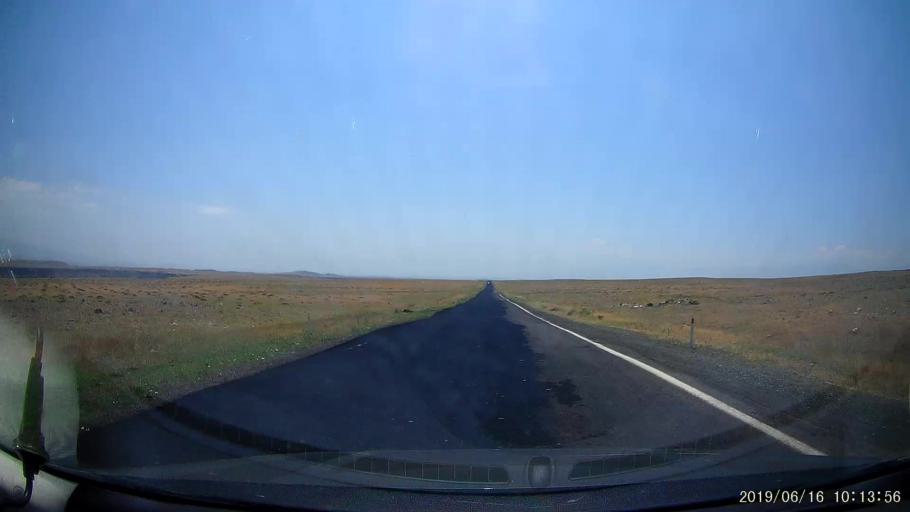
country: TR
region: Igdir
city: Tuzluca
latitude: 40.1893
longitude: 43.6523
